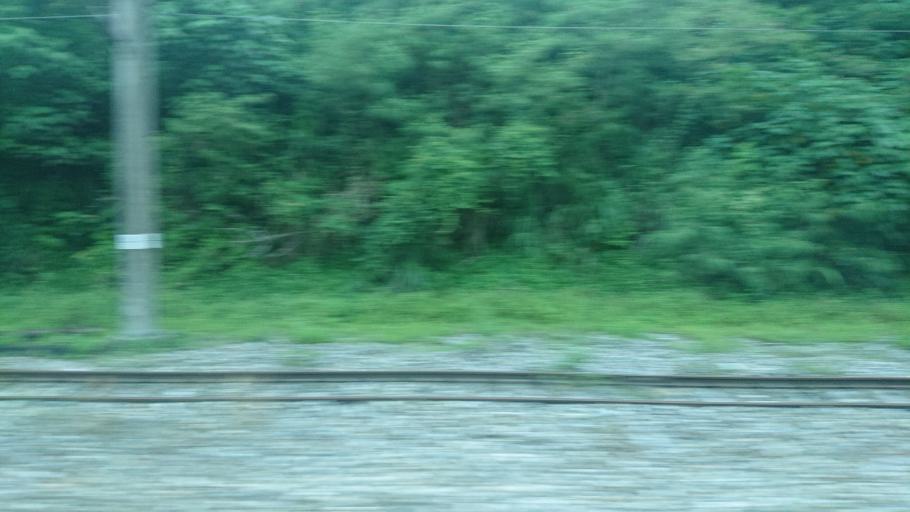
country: TW
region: Taiwan
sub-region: Hualien
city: Hualian
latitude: 24.1245
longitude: 121.6387
